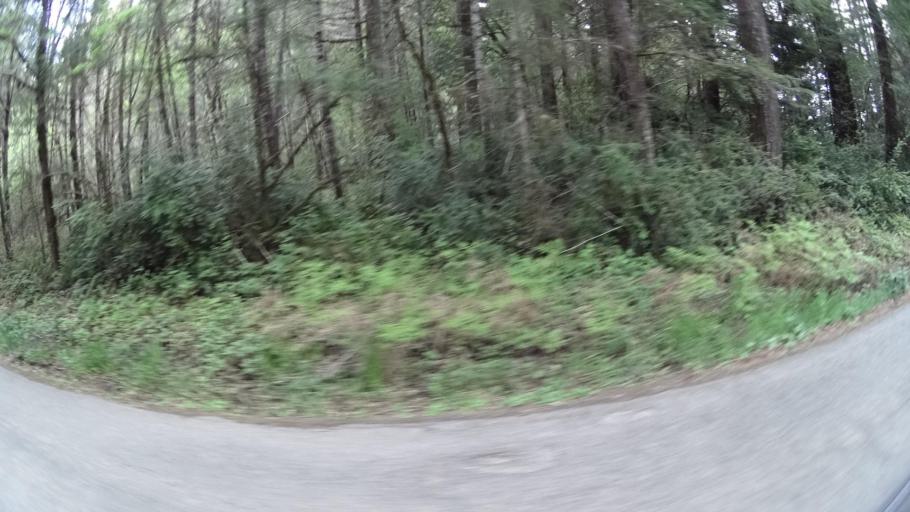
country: US
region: California
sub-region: Humboldt County
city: Redway
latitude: 40.0201
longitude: -123.9379
